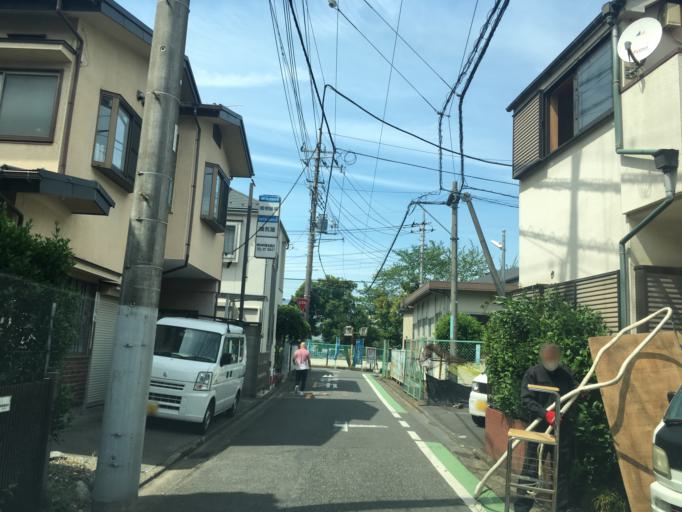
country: JP
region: Saitama
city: Tokorozawa
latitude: 35.7958
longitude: 139.4651
